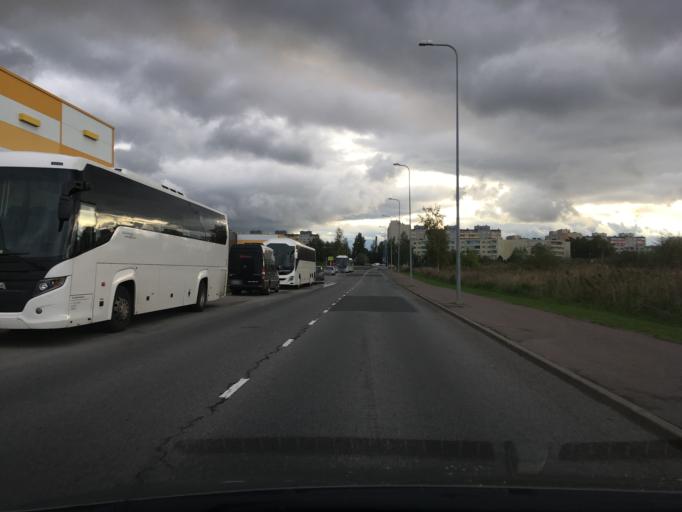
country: EE
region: Harju
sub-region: Tallinna linn
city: Kose
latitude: 59.4396
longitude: 24.8639
